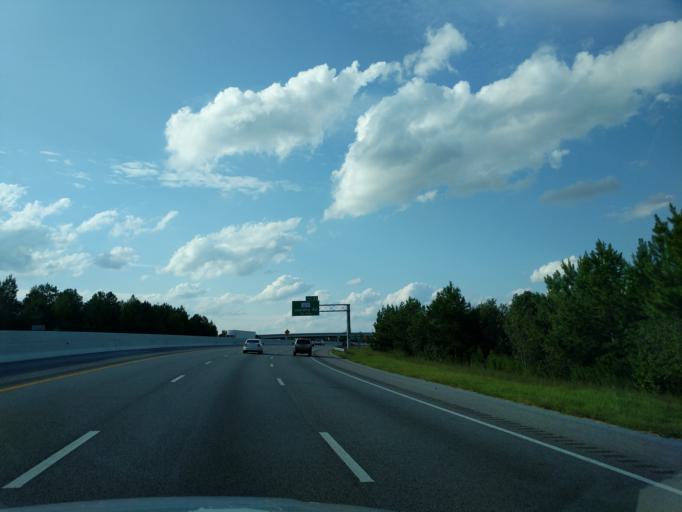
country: US
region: South Carolina
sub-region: Greenville County
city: Simpsonville
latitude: 34.7516
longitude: -82.2851
